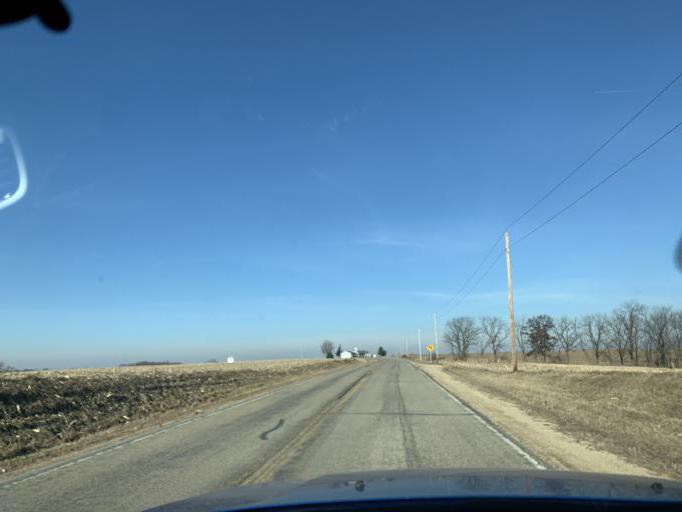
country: US
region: Wisconsin
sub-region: Iowa County
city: Barneveld
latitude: 42.8156
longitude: -89.9168
